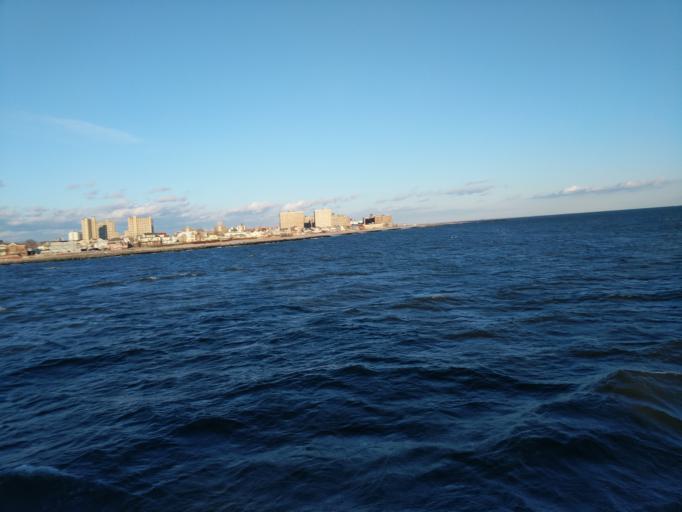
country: US
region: New York
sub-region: Kings County
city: Coney Island
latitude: 40.5737
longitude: -74.0159
